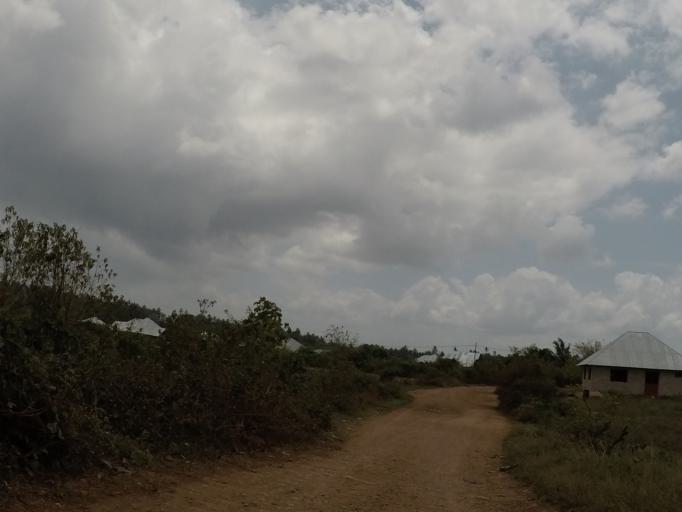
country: TZ
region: Zanzibar Central/South
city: Koani
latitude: -6.1890
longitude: 39.3085
